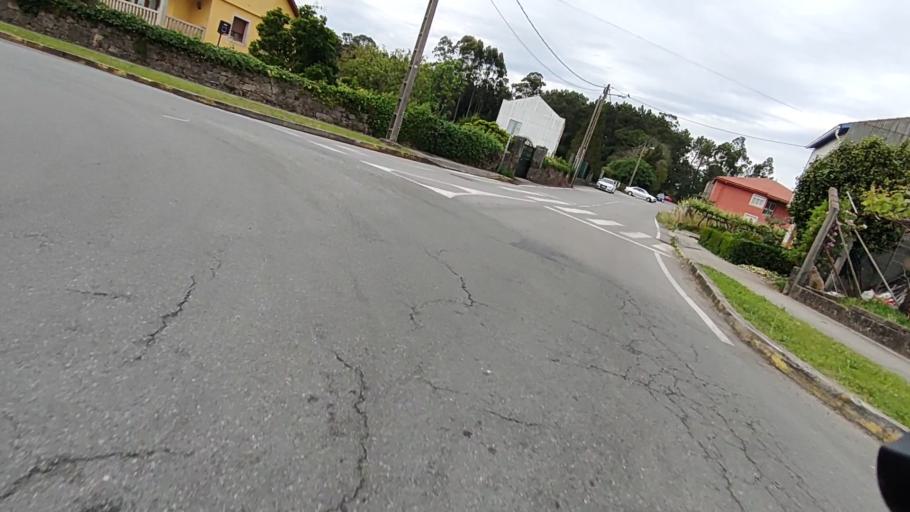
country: ES
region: Galicia
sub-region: Provincia da Coruna
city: Boiro
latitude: 42.6345
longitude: -8.8670
